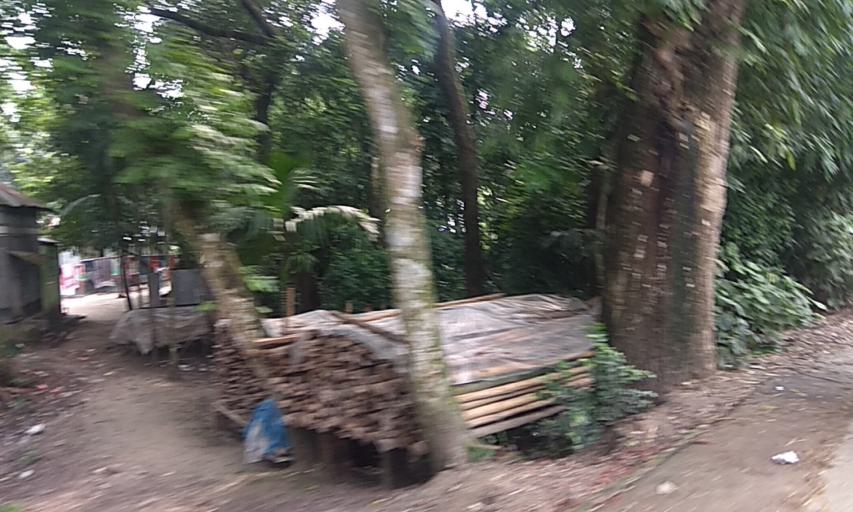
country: BD
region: Dhaka
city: Dohar
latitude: 23.4752
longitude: 90.0305
